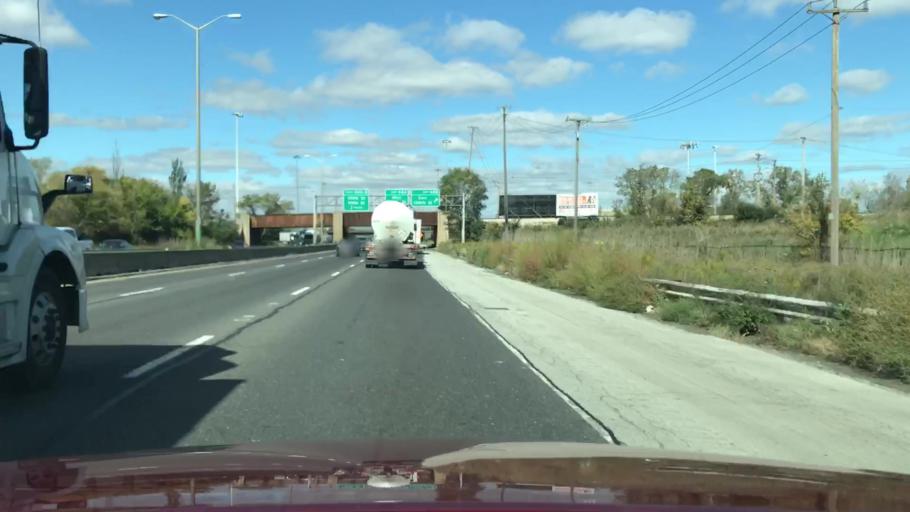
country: US
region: Illinois
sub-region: Cook County
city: Dolton
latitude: 41.6568
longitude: -87.5859
